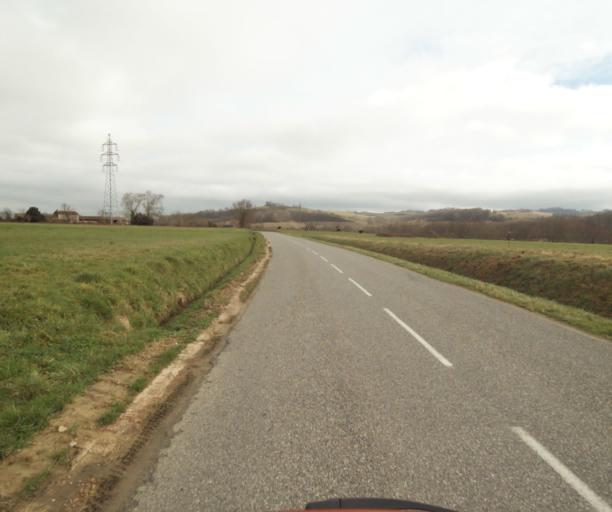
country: FR
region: Midi-Pyrenees
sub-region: Departement de l'Ariege
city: Pamiers
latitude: 43.1172
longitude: 1.5468
